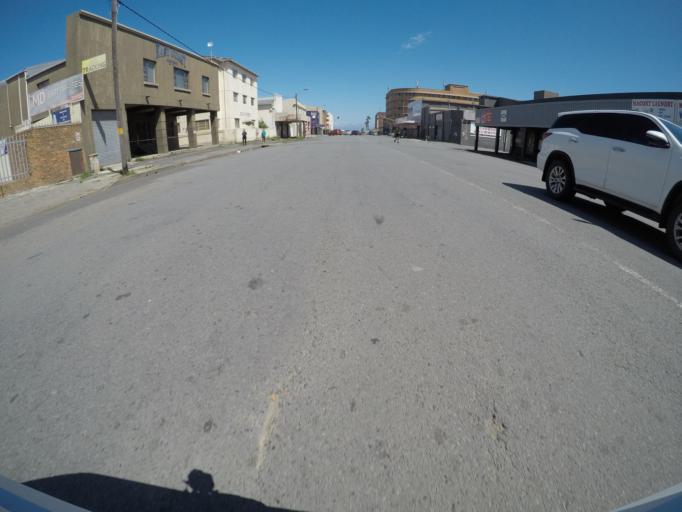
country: ZA
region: Eastern Cape
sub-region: Buffalo City Metropolitan Municipality
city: East London
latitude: -33.0166
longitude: 27.9128
